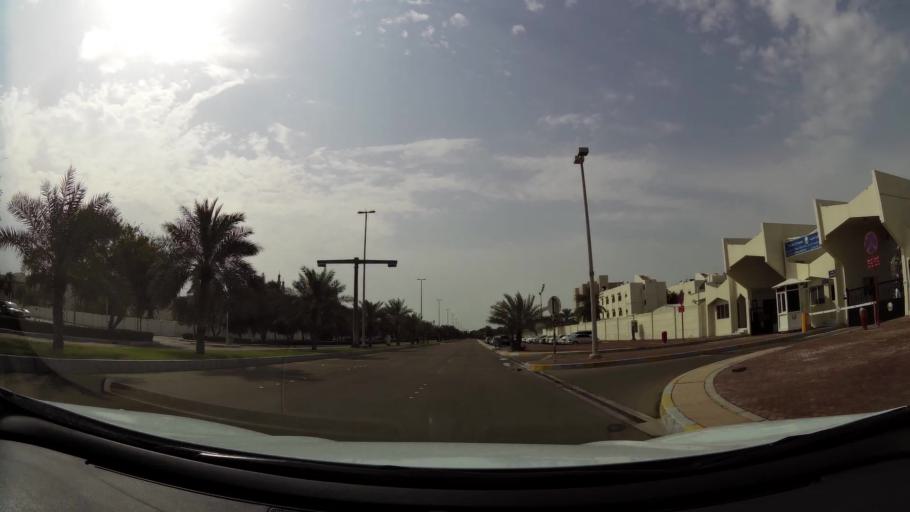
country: AE
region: Abu Dhabi
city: Abu Dhabi
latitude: 24.4403
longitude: 54.4276
